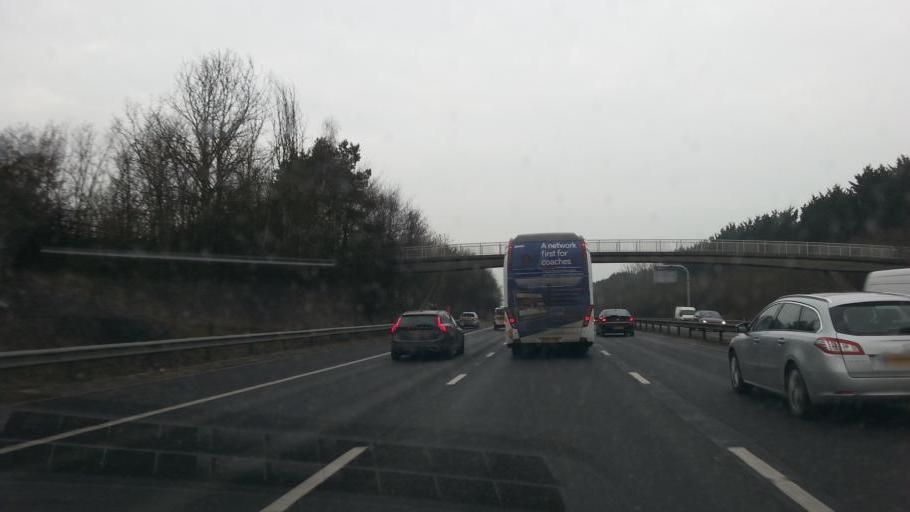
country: GB
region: England
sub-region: Hertfordshire
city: Sawbridgeworth
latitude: 51.7992
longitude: 0.1753
